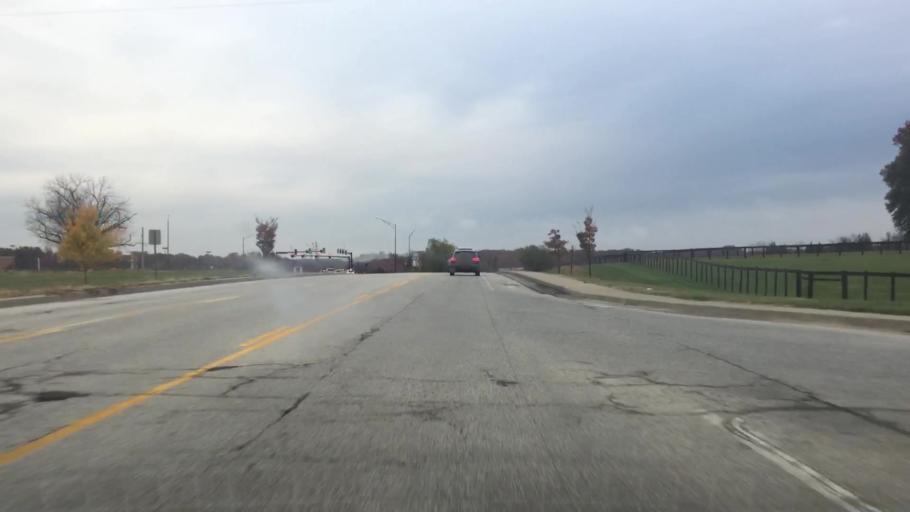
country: US
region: Missouri
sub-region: Boone County
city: Columbia
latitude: 38.9078
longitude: -92.3257
